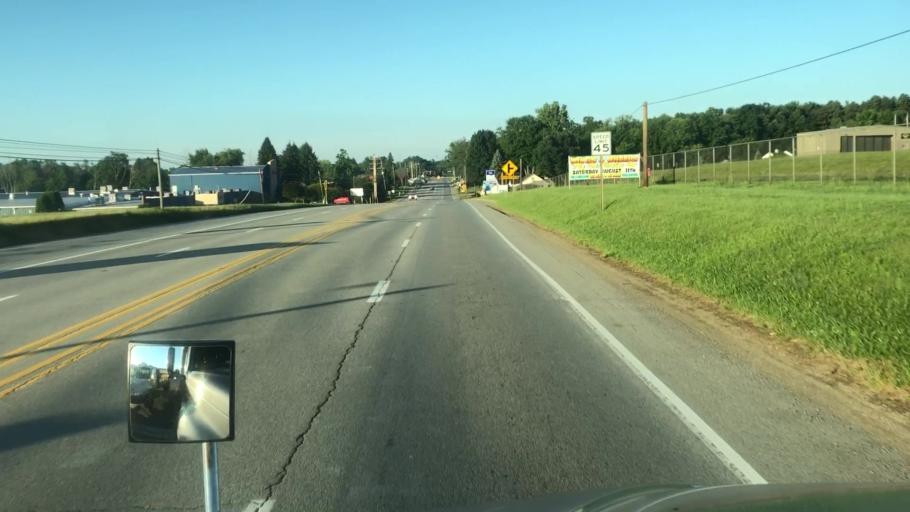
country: US
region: Pennsylvania
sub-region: Venango County
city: Franklin
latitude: 41.3782
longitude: -79.8521
